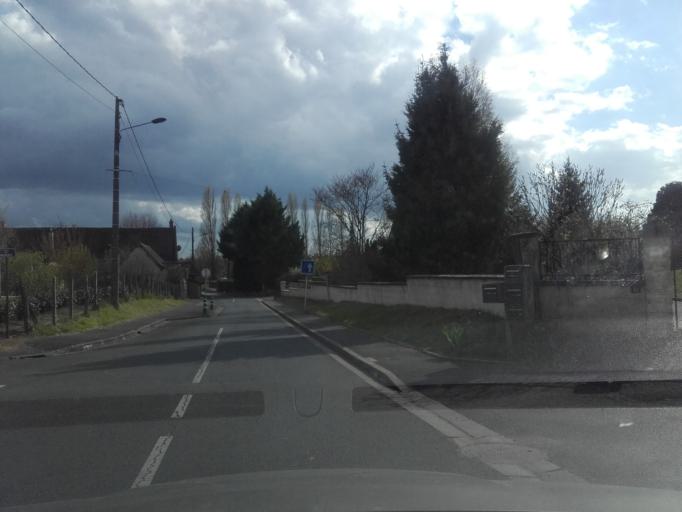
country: FR
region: Centre
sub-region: Departement d'Indre-et-Loire
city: Luynes
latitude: 47.3974
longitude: 0.5550
